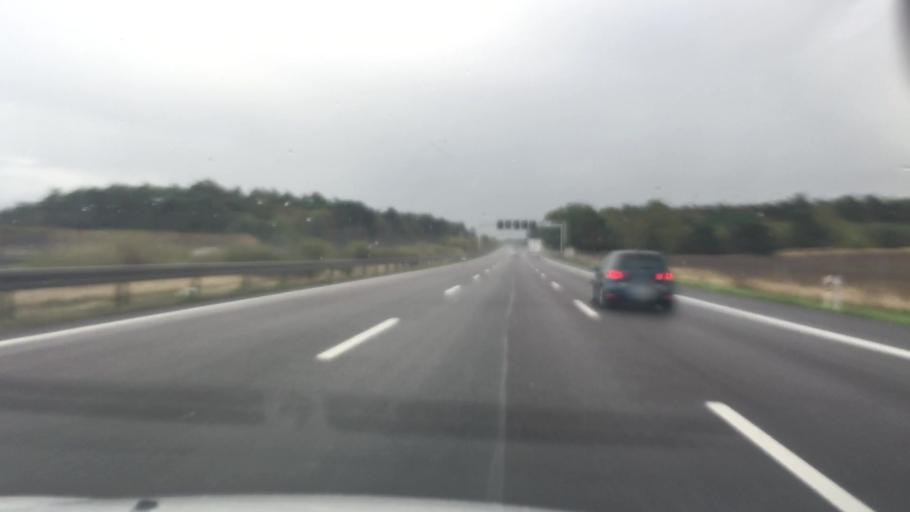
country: DE
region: Lower Saxony
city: Rennau
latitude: 52.2953
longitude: 10.8725
